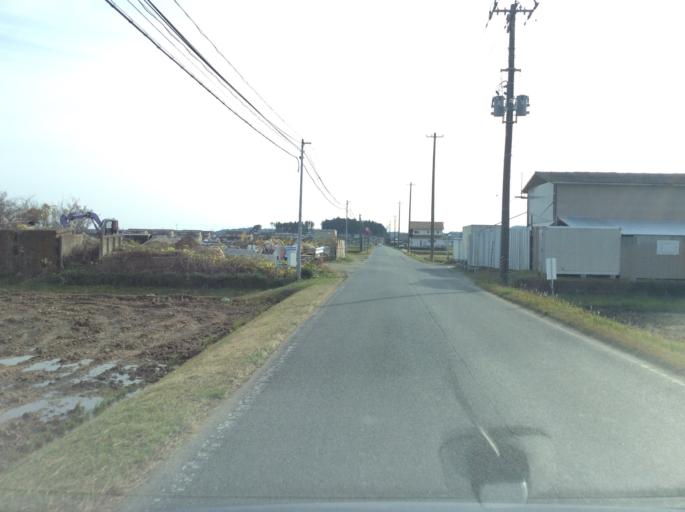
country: JP
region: Fukushima
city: Iwaki
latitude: 37.0776
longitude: 140.9423
